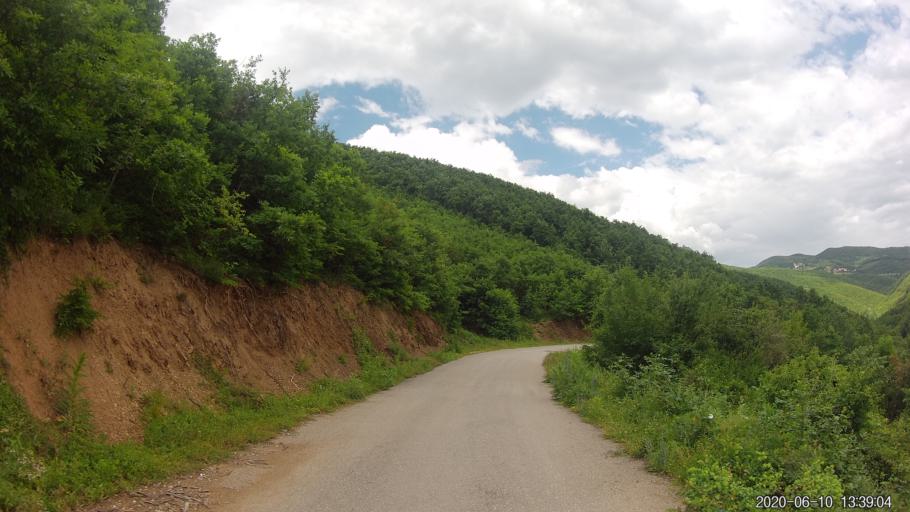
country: XK
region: Prizren
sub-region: Komuna e Therandes
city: Budakovo
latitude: 42.4122
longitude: 20.9091
